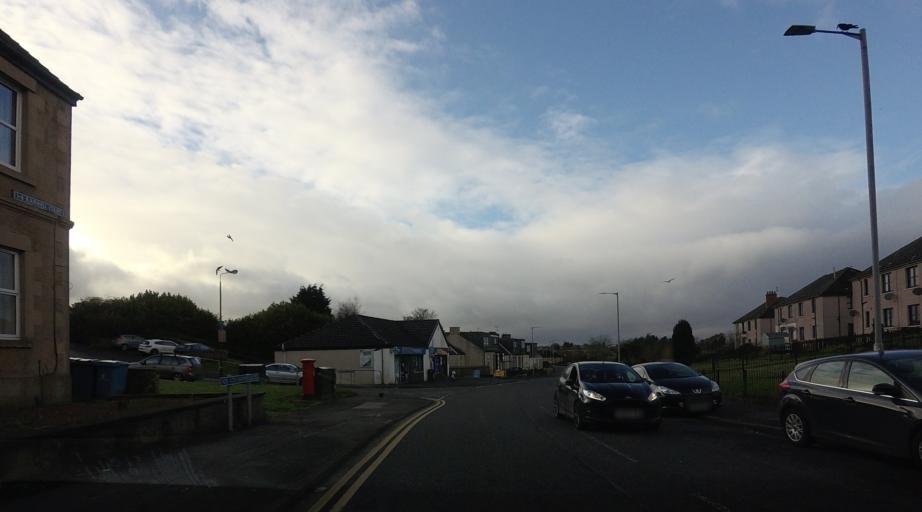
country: GB
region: Scotland
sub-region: Falkirk
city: Polmont
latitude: 55.9747
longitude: -3.7078
